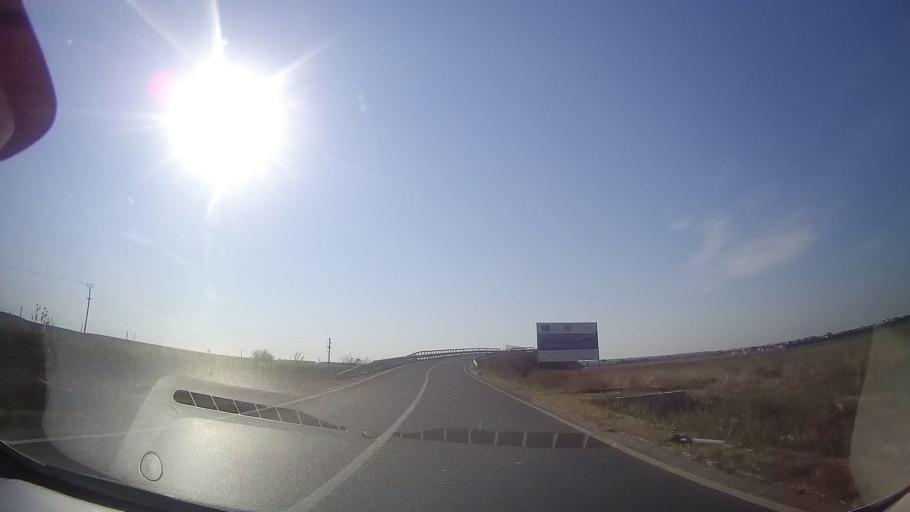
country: RO
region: Timis
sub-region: Oras Recas
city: Recas
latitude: 45.8145
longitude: 21.5278
